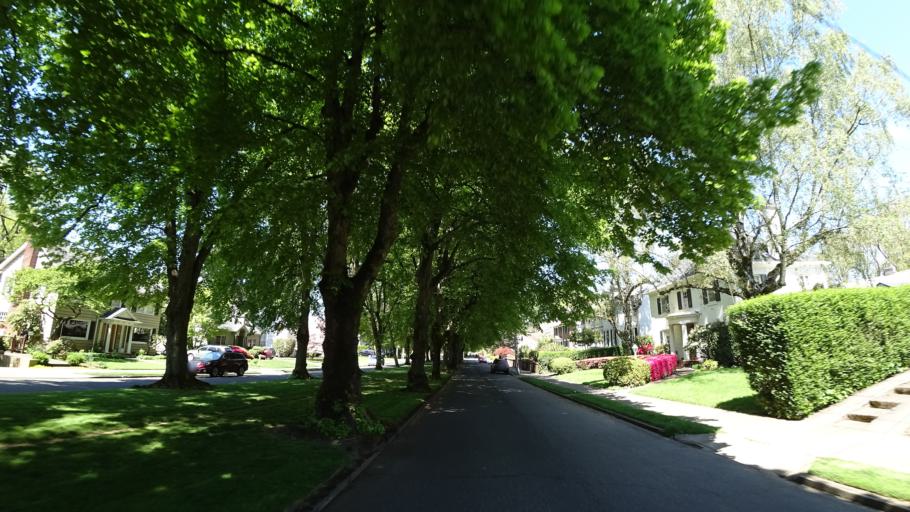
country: US
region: Oregon
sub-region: Clackamas County
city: Milwaukie
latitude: 45.4757
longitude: -122.6293
